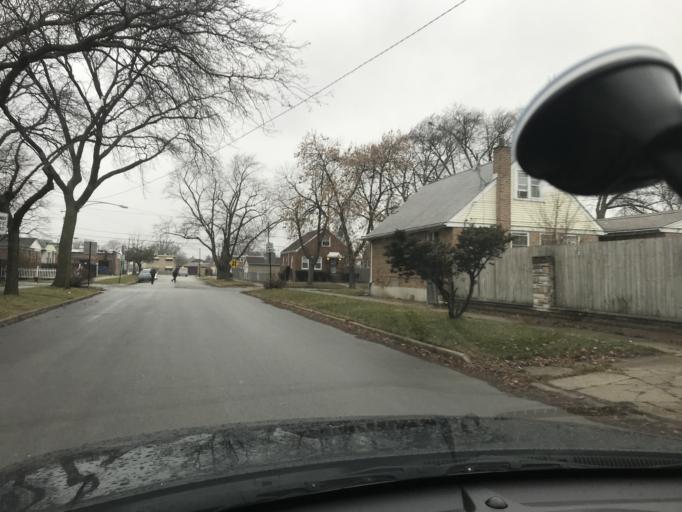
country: US
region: Illinois
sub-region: Cook County
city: Evergreen Park
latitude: 41.7250
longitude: -87.6414
